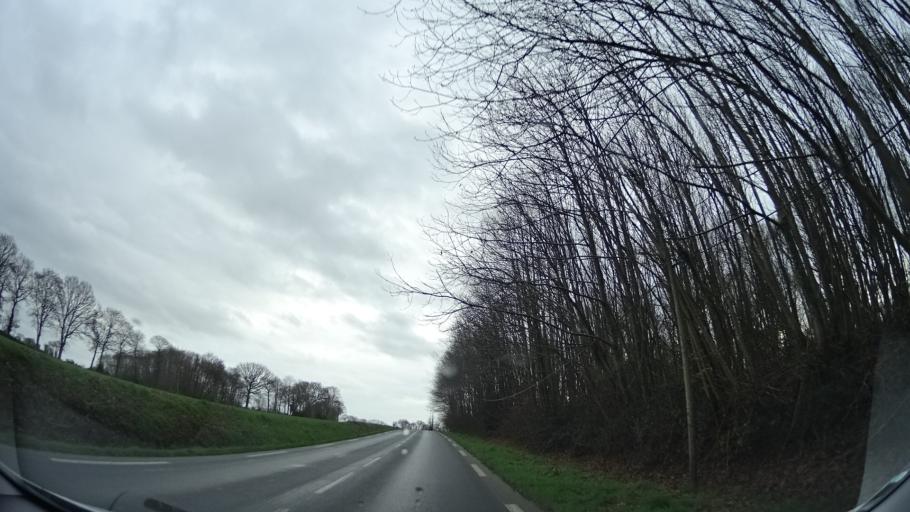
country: FR
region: Brittany
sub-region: Departement des Cotes-d'Armor
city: Les Champs-Geraux
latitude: 48.4034
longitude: -1.9823
